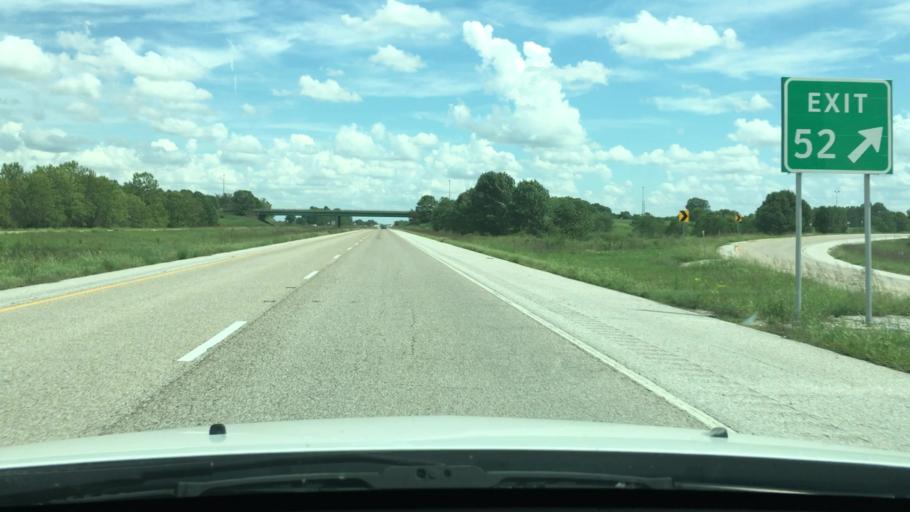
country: US
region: Illinois
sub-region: Scott County
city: Winchester
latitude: 39.6810
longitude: -90.4609
